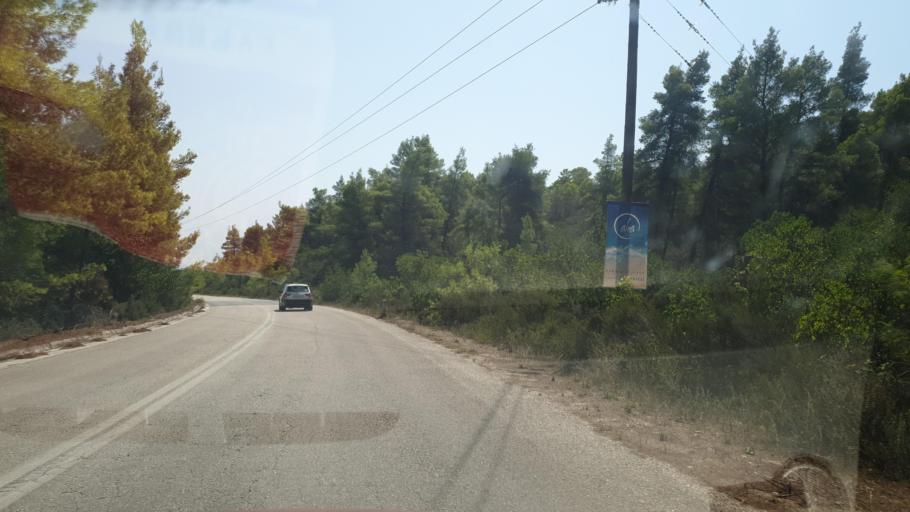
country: GR
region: Central Macedonia
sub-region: Nomos Chalkidikis
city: Sarti
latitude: 40.1311
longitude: 23.9282
